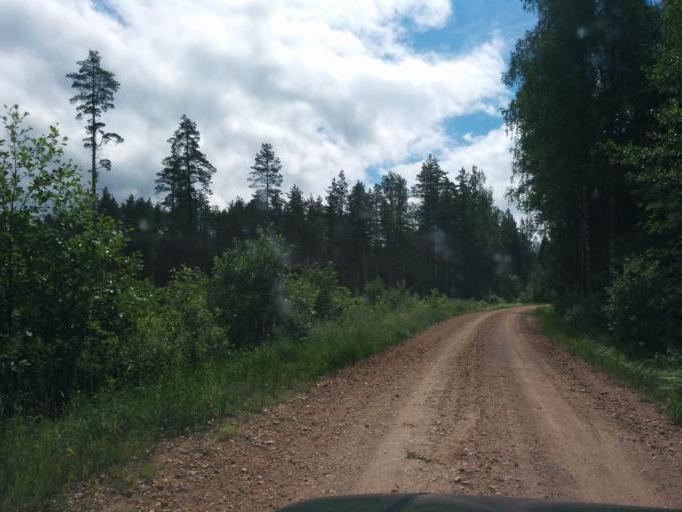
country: LV
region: Vilaka
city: Vilaka
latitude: 57.3727
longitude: 27.6711
